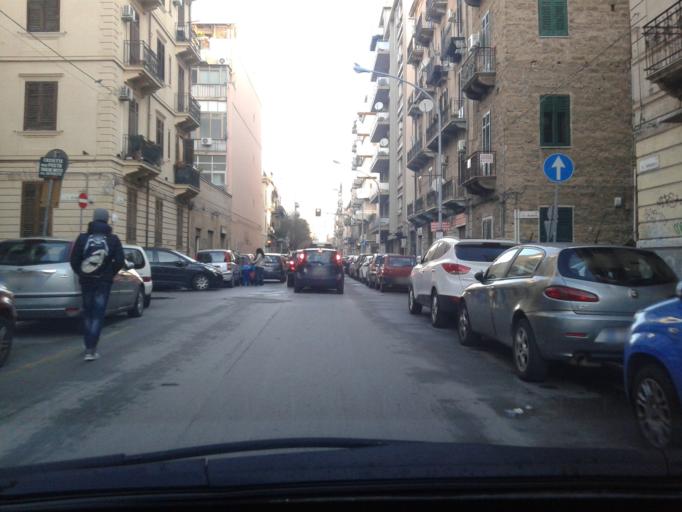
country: IT
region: Sicily
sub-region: Palermo
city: Palermo
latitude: 38.1215
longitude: 13.3449
